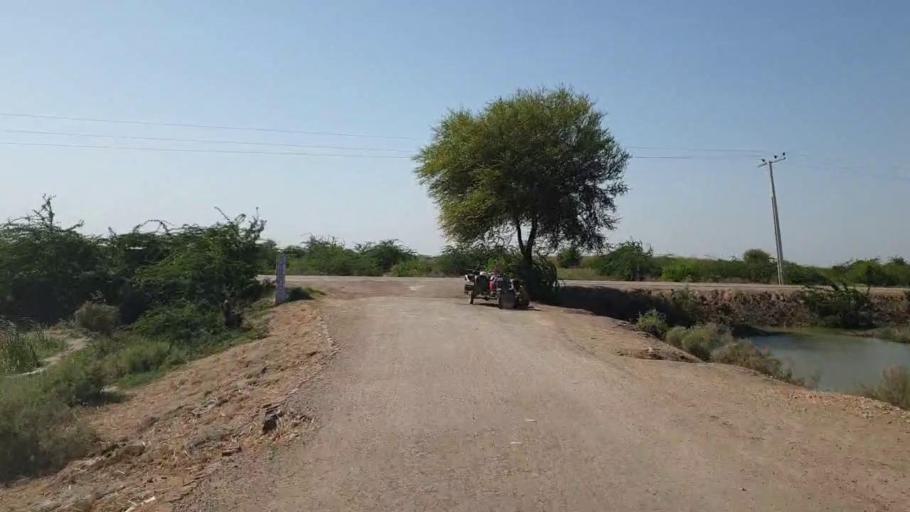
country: PK
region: Sindh
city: Tando Bago
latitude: 24.7056
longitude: 69.0109
